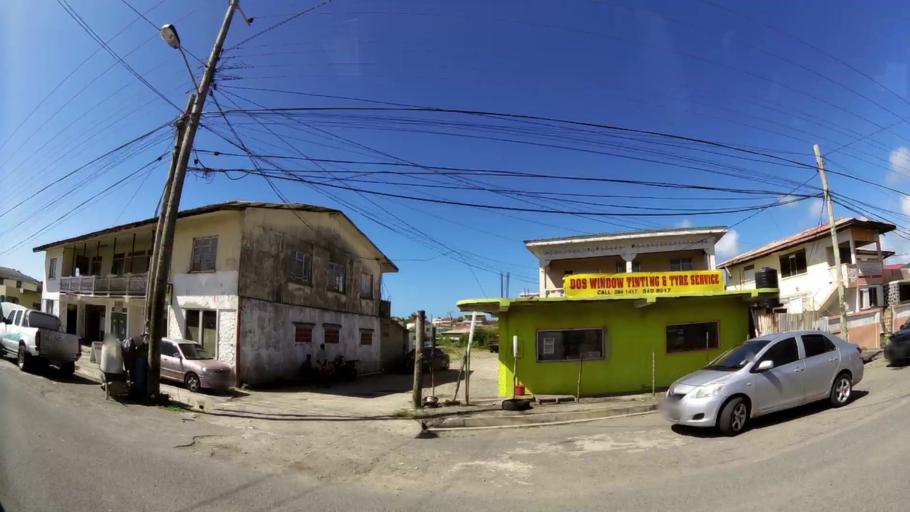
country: LC
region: Vieux-Fort
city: Vieux Fort
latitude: 13.7287
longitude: -60.9517
